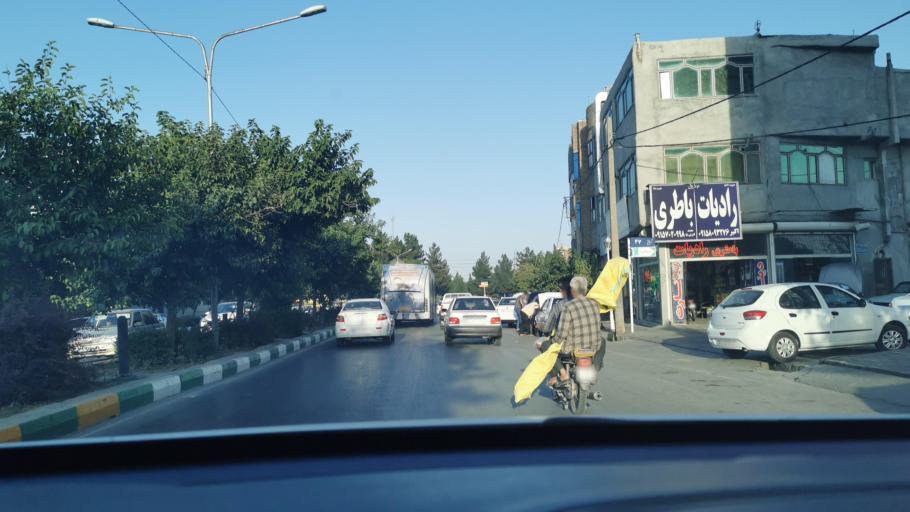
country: IR
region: Razavi Khorasan
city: Mashhad
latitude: 36.2886
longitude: 59.6566
